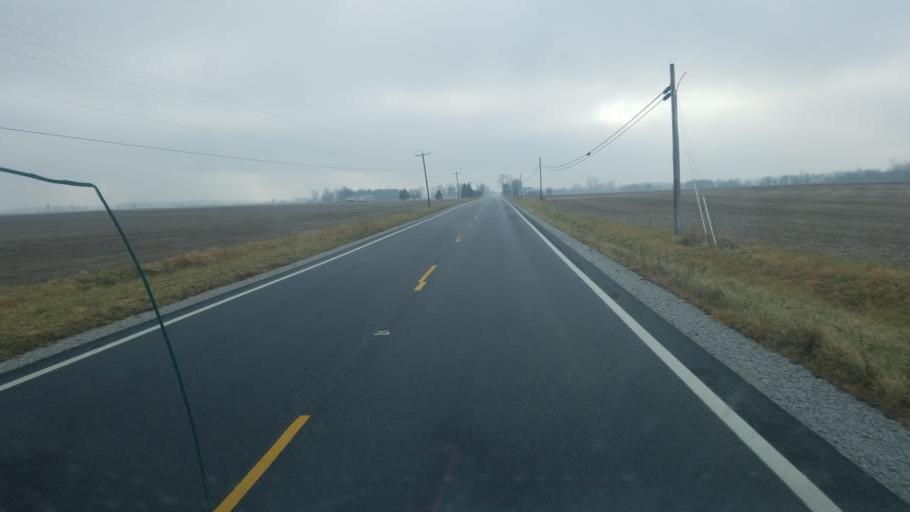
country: US
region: Ohio
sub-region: Hardin County
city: Kenton
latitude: 40.6792
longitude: -83.5163
